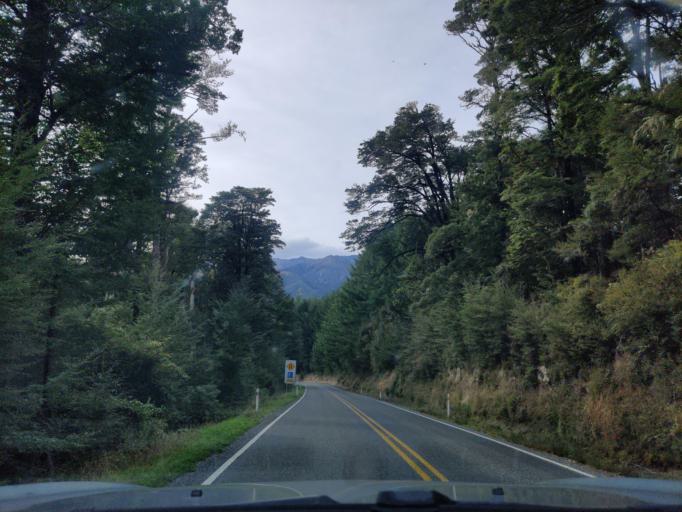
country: NZ
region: Tasman
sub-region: Tasman District
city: Wakefield
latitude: -41.7689
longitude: 172.9528
